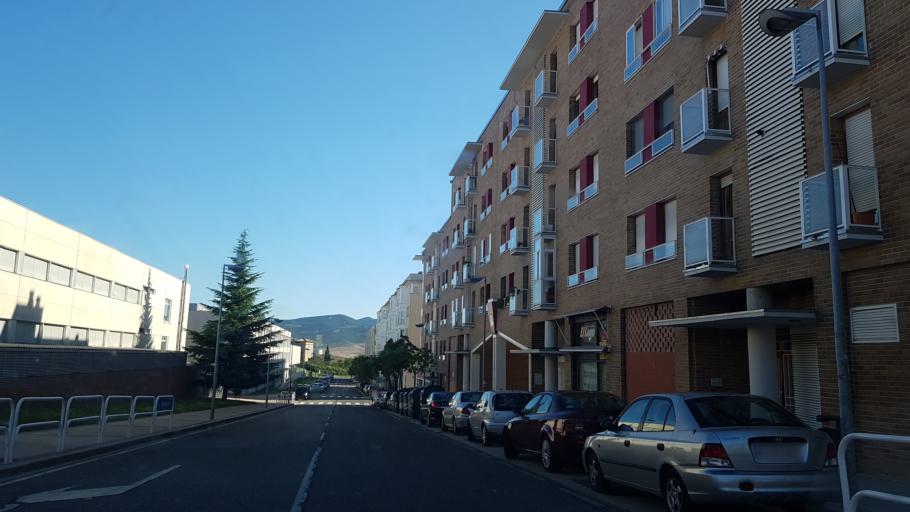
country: ES
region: Navarre
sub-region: Provincia de Navarra
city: Burlata
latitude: 42.8077
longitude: -1.6164
